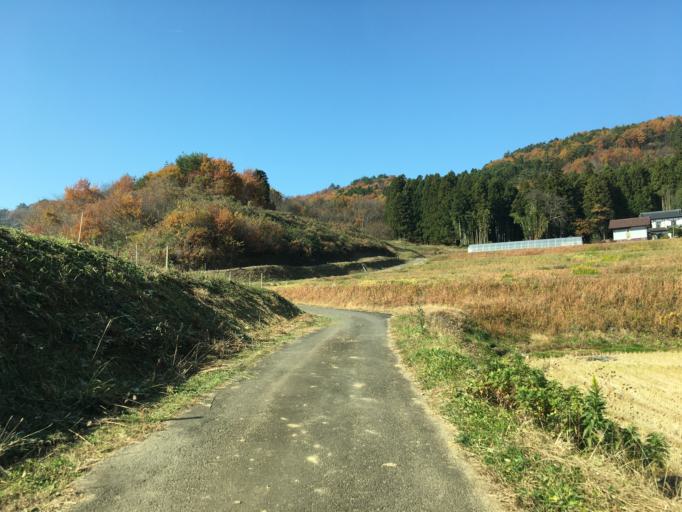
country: JP
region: Fukushima
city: Nihommatsu
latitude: 37.5754
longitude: 140.3749
